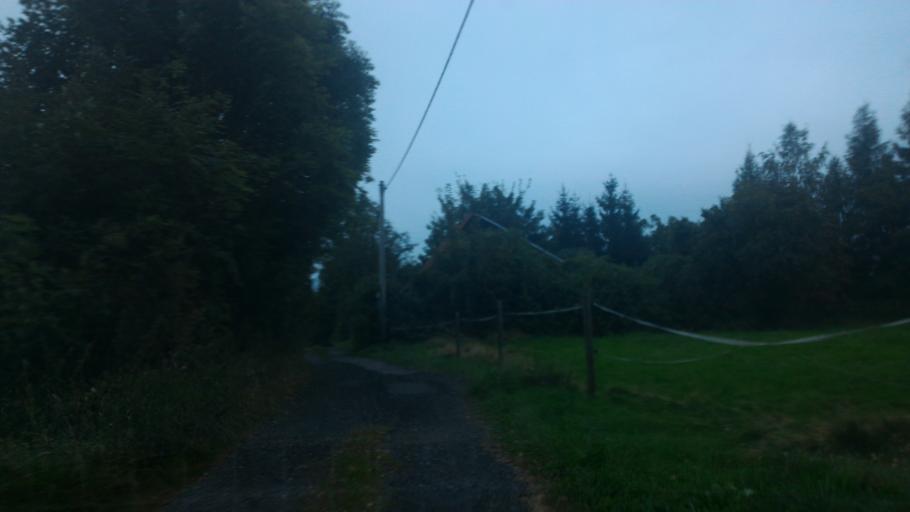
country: CZ
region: Ustecky
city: Dolni Podluzi
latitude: 50.9044
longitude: 14.5754
